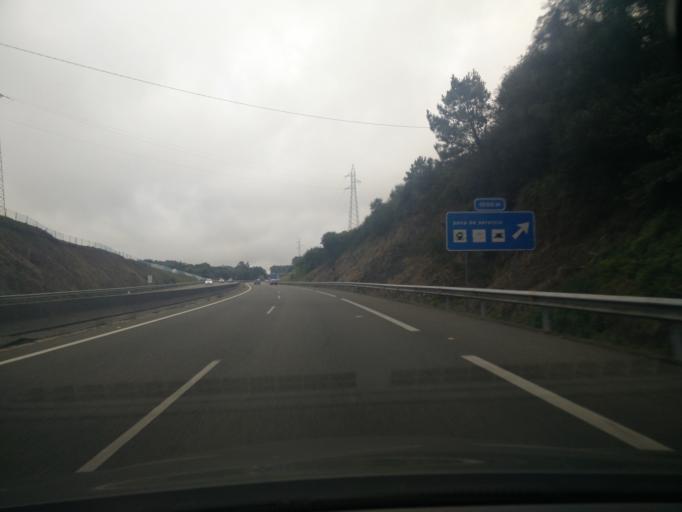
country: ES
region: Galicia
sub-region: Provincia da Coruna
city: Arteixo
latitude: 43.2682
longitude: -8.5373
